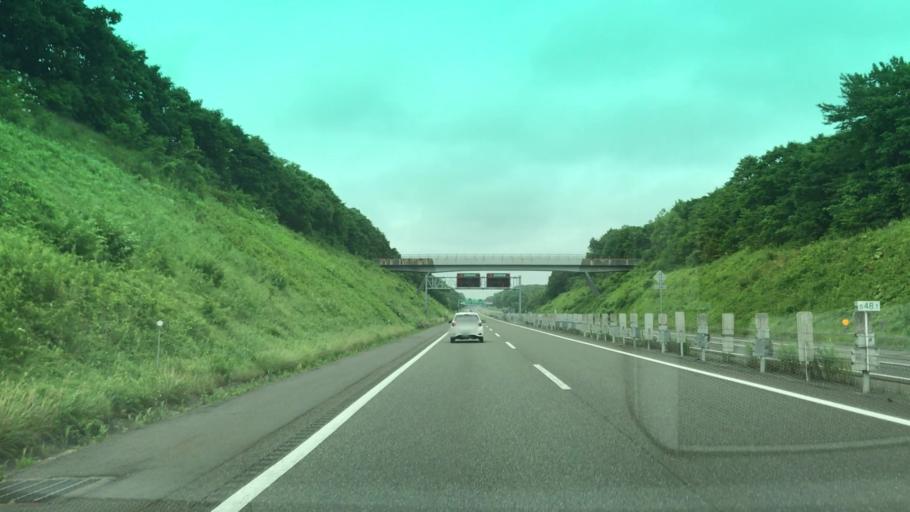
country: JP
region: Hokkaido
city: Tomakomai
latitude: 42.7015
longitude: 141.6515
